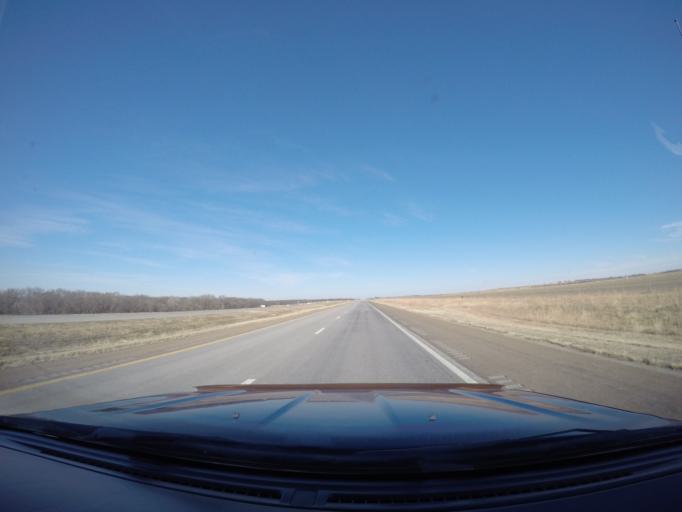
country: US
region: Kansas
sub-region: Cloud County
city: Concordia
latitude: 39.6195
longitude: -97.6601
